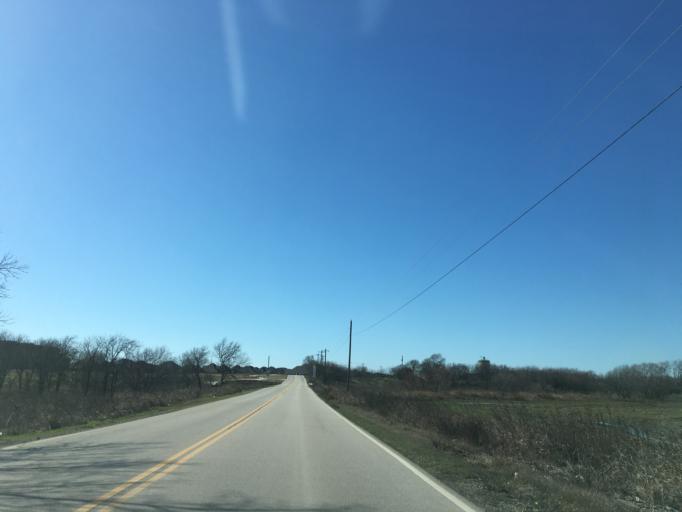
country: US
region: Texas
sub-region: Collin County
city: Prosper
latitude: 33.2311
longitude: -96.8410
